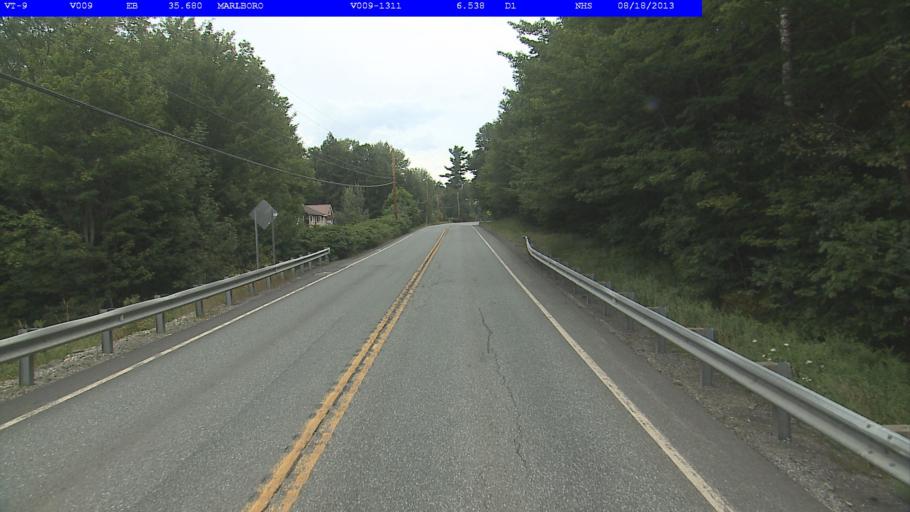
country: US
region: Vermont
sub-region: Windham County
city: West Brattleboro
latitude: 42.8783
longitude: -72.7084
